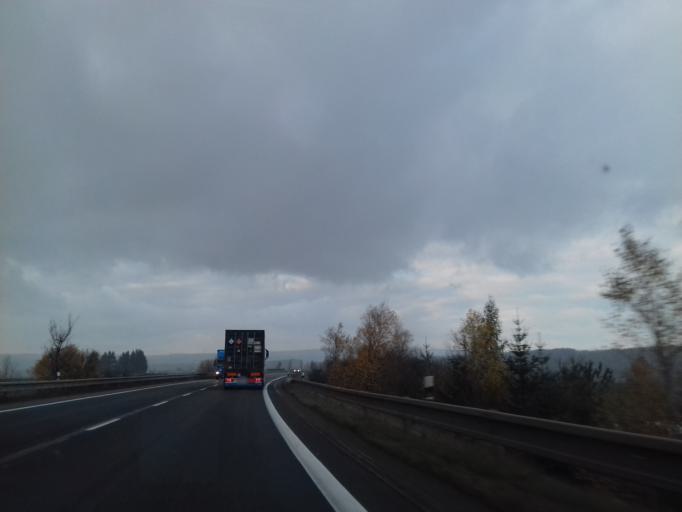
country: CZ
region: Pardubicky
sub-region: Okres Svitavy
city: Svitavy
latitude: 49.7583
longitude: 16.5409
